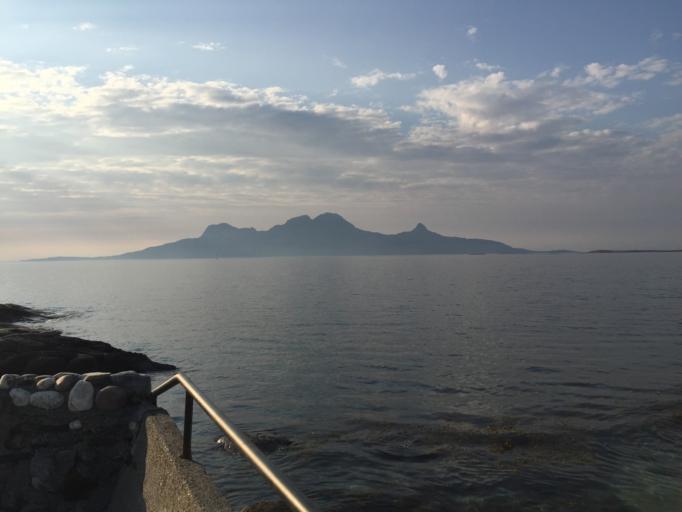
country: NO
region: Nordland
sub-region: Bodo
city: Lopsmarka
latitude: 67.3453
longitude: 14.5196
